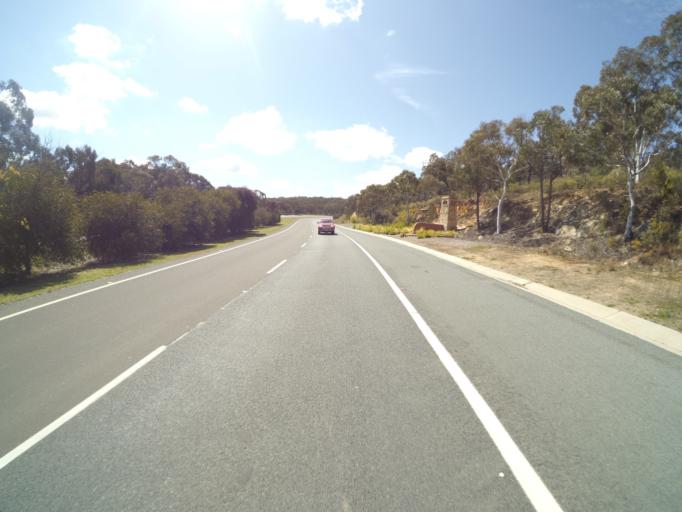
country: AU
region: New South Wales
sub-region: Goulburn Mulwaree
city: Goulburn
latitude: -34.7442
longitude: 149.7575
